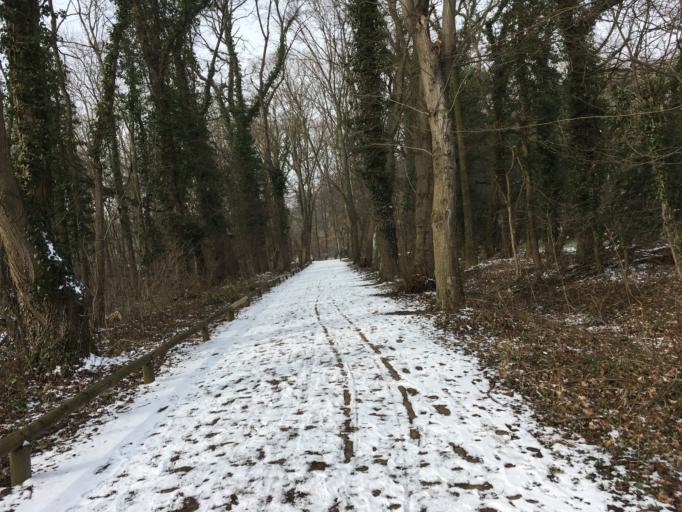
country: DE
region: North Rhine-Westphalia
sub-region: Regierungsbezirk Koln
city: Dueren
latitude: 50.7797
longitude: 6.4915
